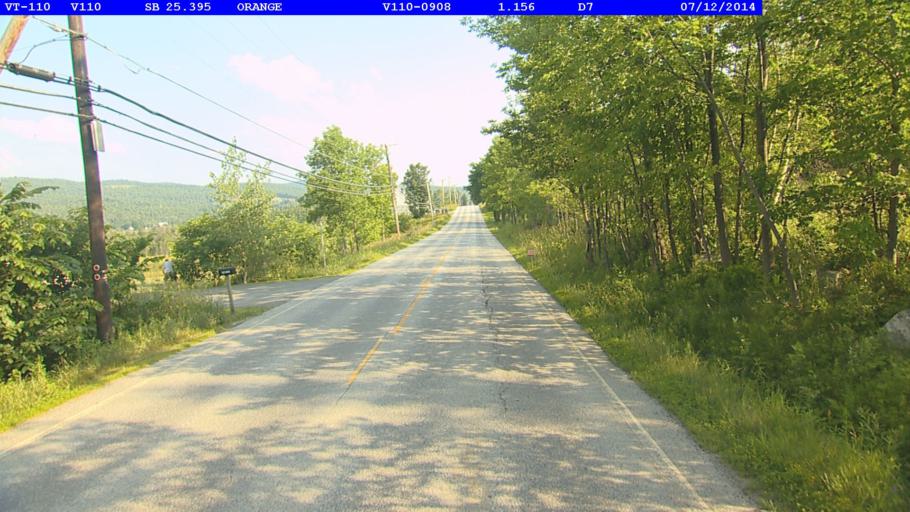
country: US
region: Vermont
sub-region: Washington County
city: South Barre
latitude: 44.1406
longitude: -72.4333
